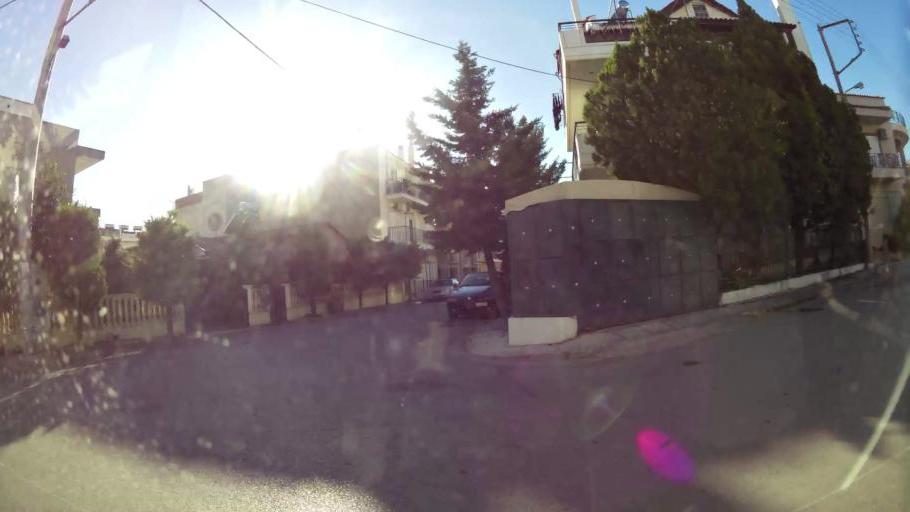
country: GR
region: Attica
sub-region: Nomarchia Anatolikis Attikis
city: Acharnes
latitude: 38.0853
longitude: 23.7289
